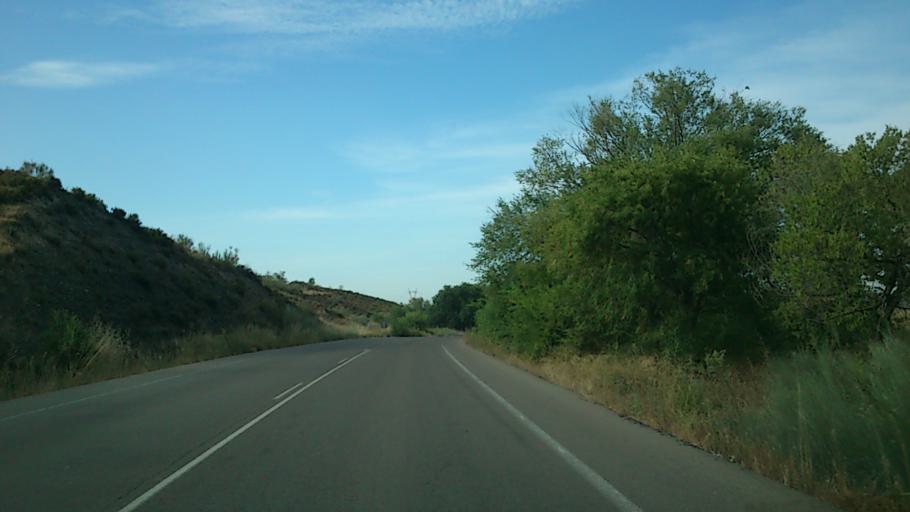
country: ES
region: Aragon
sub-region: Provincia de Zaragoza
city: San Mateo de Gallego
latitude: 41.8008
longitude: -0.7783
